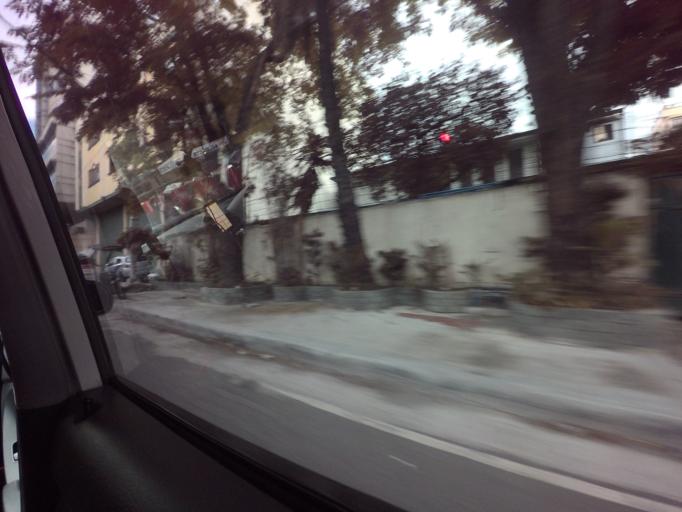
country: PH
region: Calabarzon
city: Del Monte
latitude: 14.6175
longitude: 121.0080
